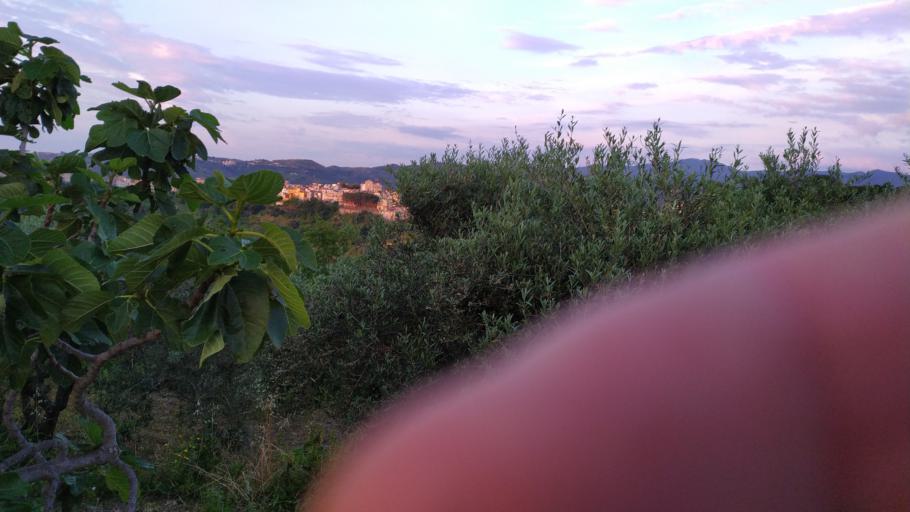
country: IT
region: Sicily
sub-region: Messina
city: San Pier Niceto
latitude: 38.1588
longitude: 15.3390
